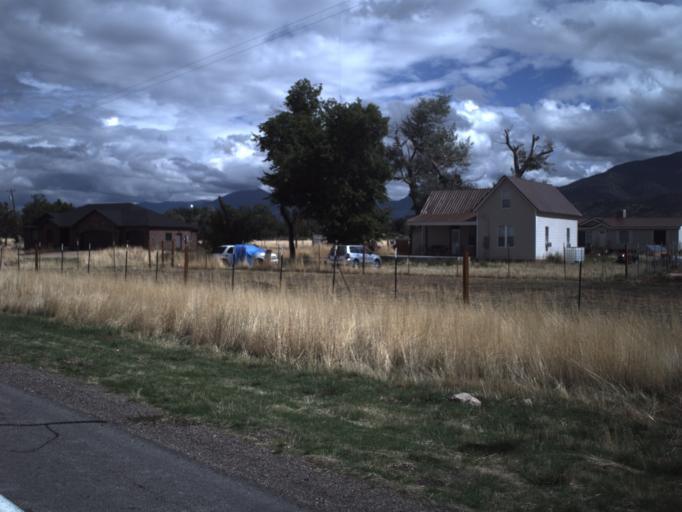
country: US
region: Utah
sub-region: Millard County
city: Fillmore
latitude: 38.8807
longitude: -112.4111
